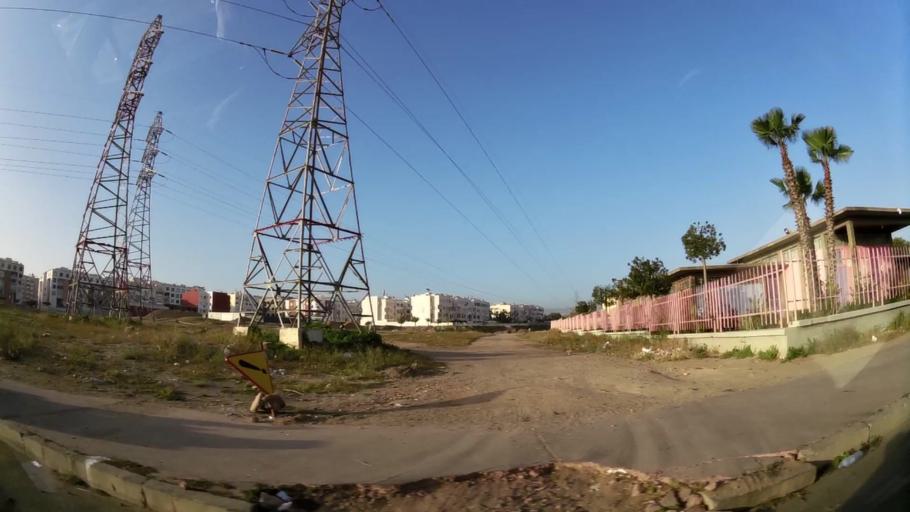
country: MA
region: Oued ed Dahab-Lagouira
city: Dakhla
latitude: 30.4156
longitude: -9.5629
